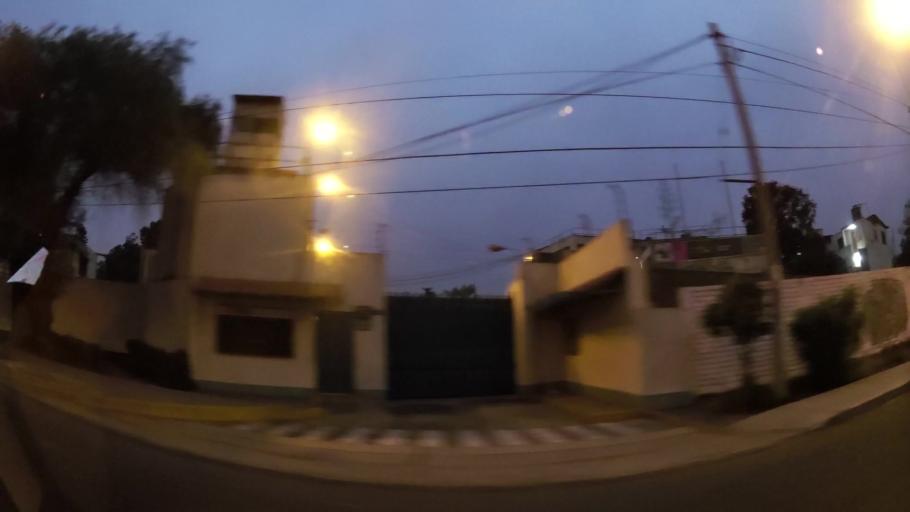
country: PE
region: Lima
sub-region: Lima
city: La Molina
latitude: -12.0779
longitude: -76.9542
